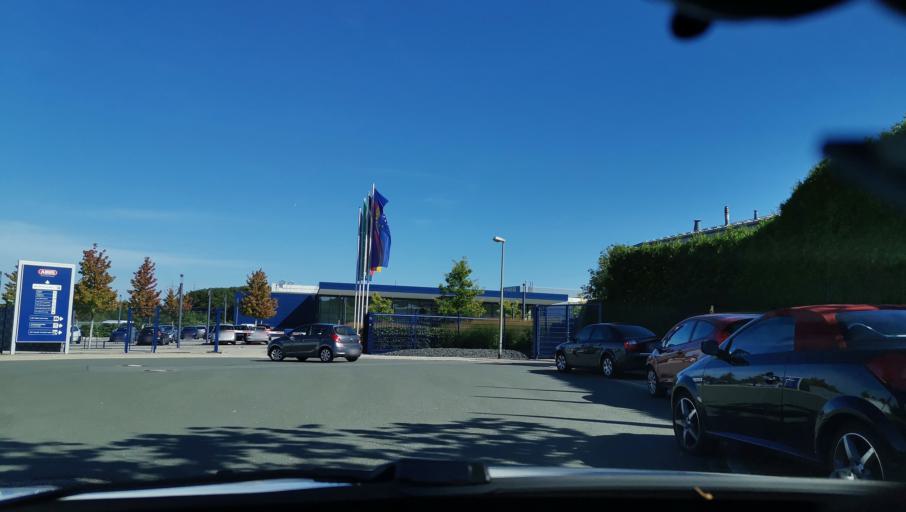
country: DE
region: North Rhine-Westphalia
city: Wetter (Ruhr)
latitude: 51.3581
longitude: 7.3819
